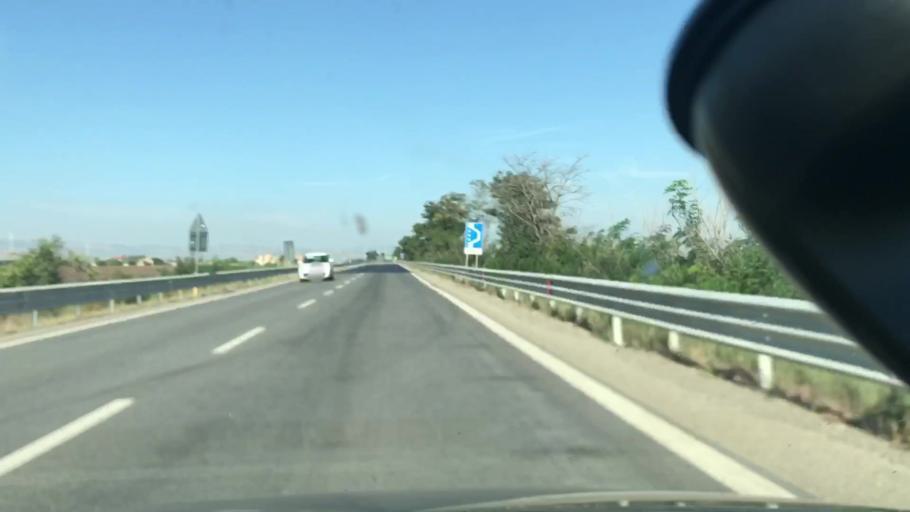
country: IT
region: Basilicate
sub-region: Provincia di Potenza
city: Melfi
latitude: 41.0719
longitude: 15.6521
